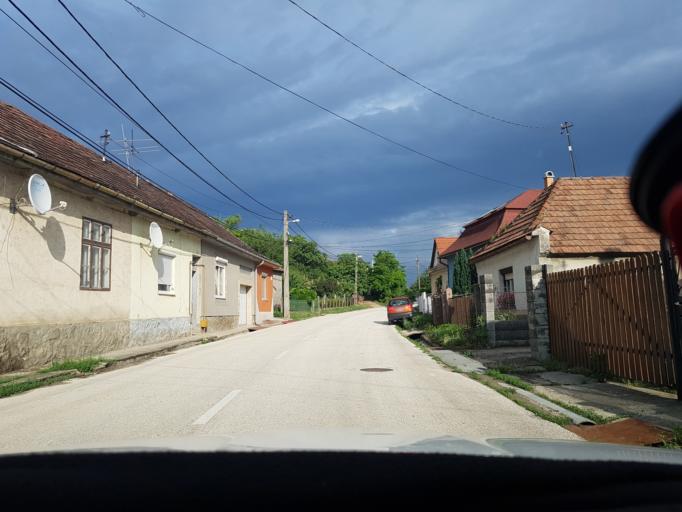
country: HU
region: Komarom-Esztergom
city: Labatlan
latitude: 47.7390
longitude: 18.5114
